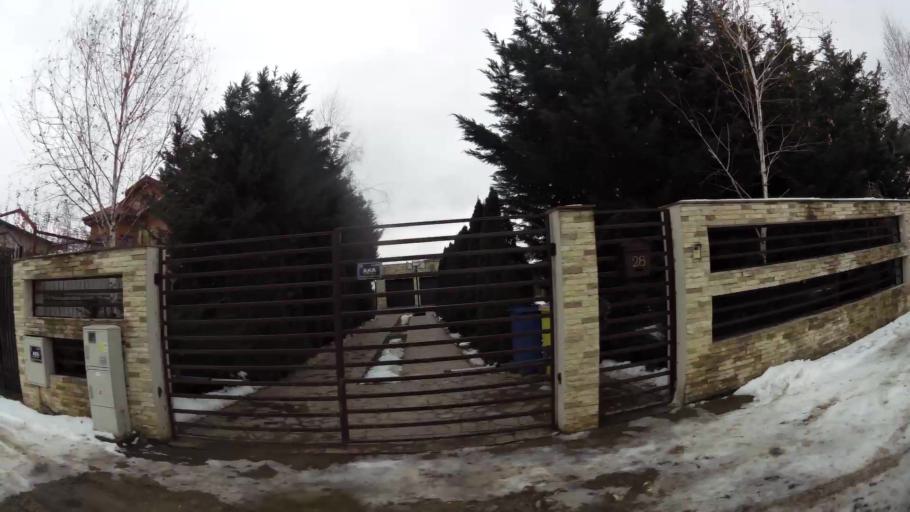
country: RO
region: Ilfov
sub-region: Comuna Otopeni
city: Otopeni
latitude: 44.5548
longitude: 26.1021
